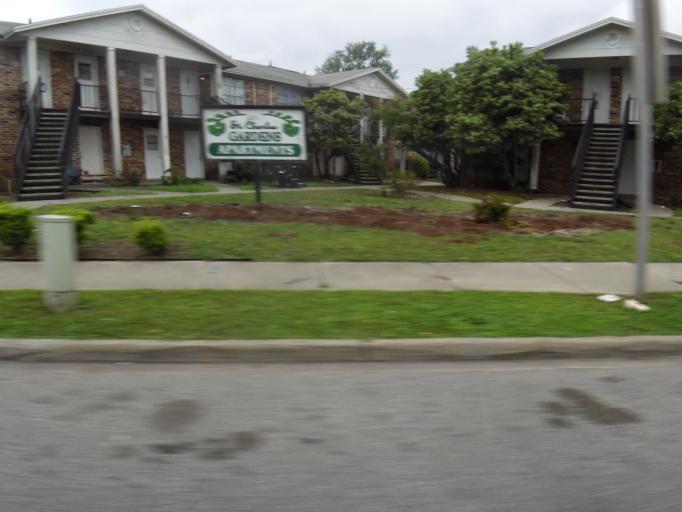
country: US
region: Florida
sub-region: Duval County
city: Jacksonville
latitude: 30.3028
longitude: -81.6347
